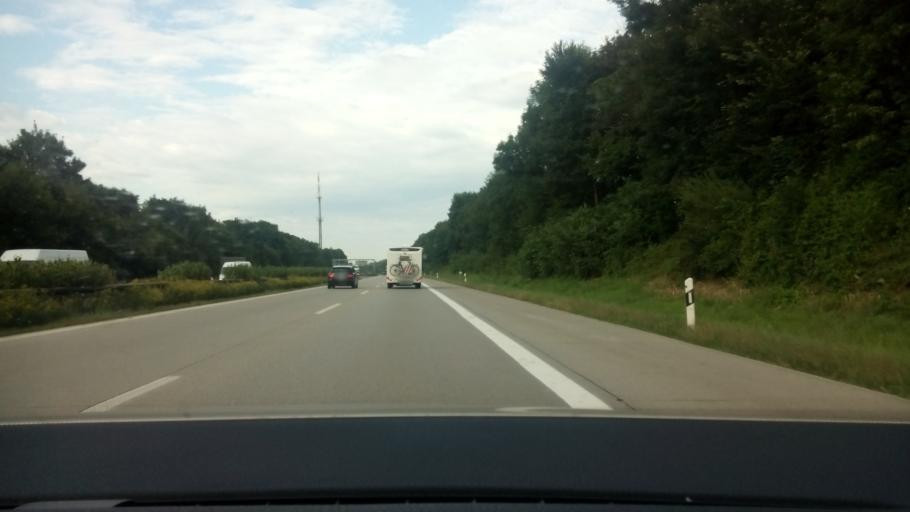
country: DE
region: Bavaria
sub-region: Upper Bavaria
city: Unterschleissheim
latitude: 48.2908
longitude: 11.5675
